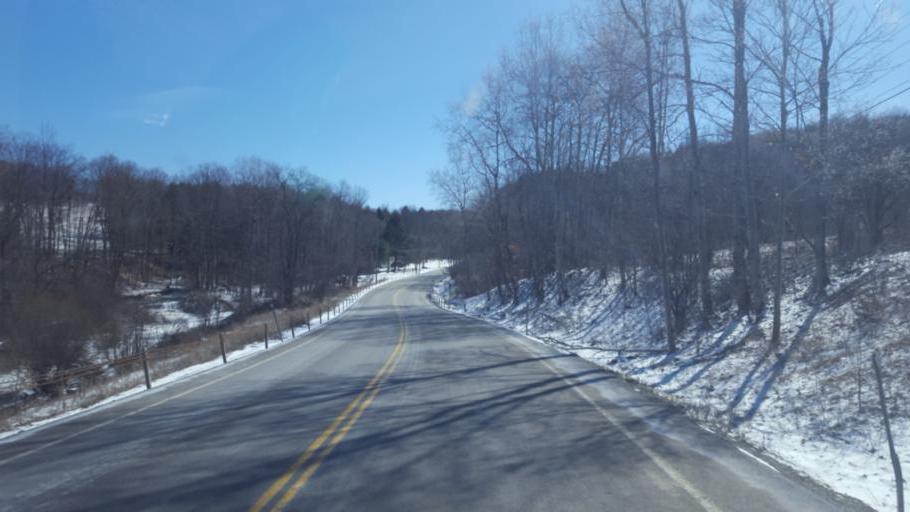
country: US
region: New York
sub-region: Allegany County
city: Andover
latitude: 42.0699
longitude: -77.8419
